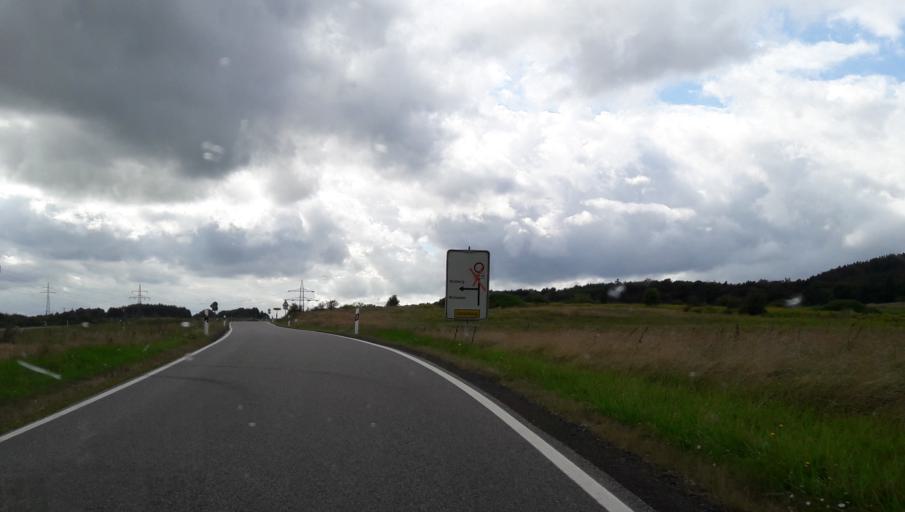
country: DE
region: Saarland
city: Nohfelden
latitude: 49.5606
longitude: 7.1556
